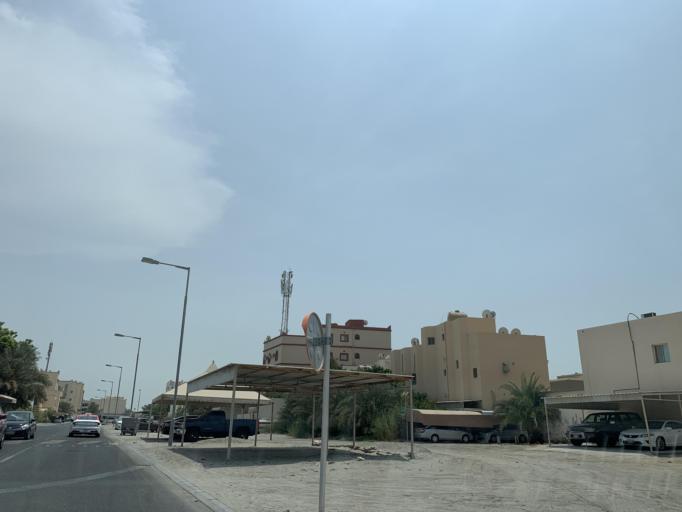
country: BH
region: Muharraq
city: Al Hadd
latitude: 26.2783
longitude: 50.6450
